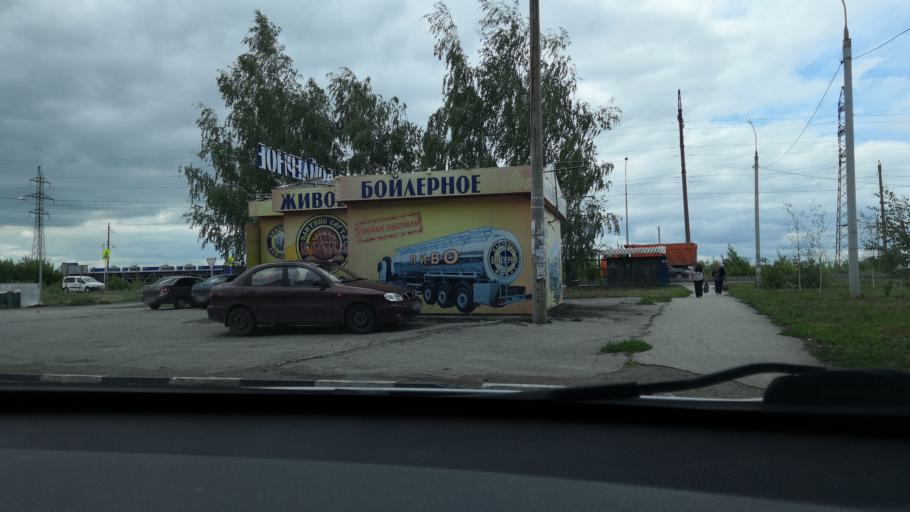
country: RU
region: Samara
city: Smyshlyayevka
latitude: 53.2692
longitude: 50.3872
